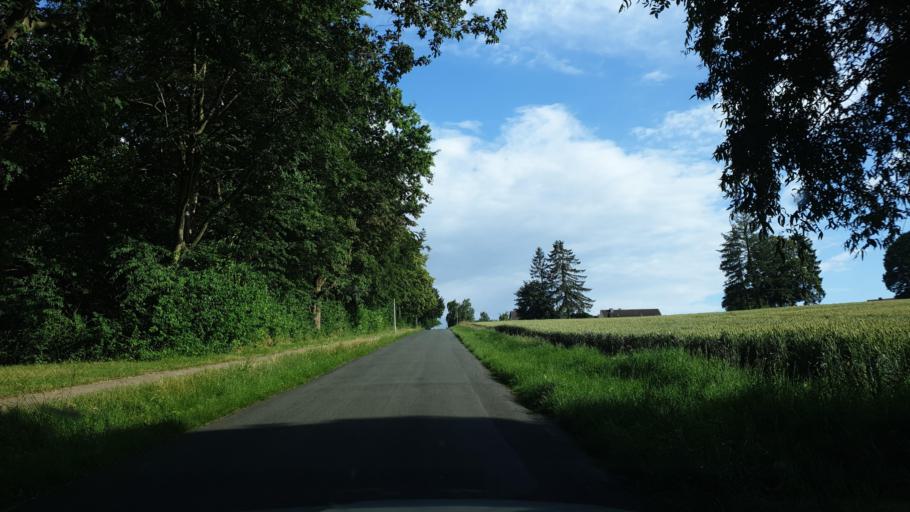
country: DE
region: North Rhine-Westphalia
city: Bad Oeynhausen
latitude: 52.1843
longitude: 8.7935
